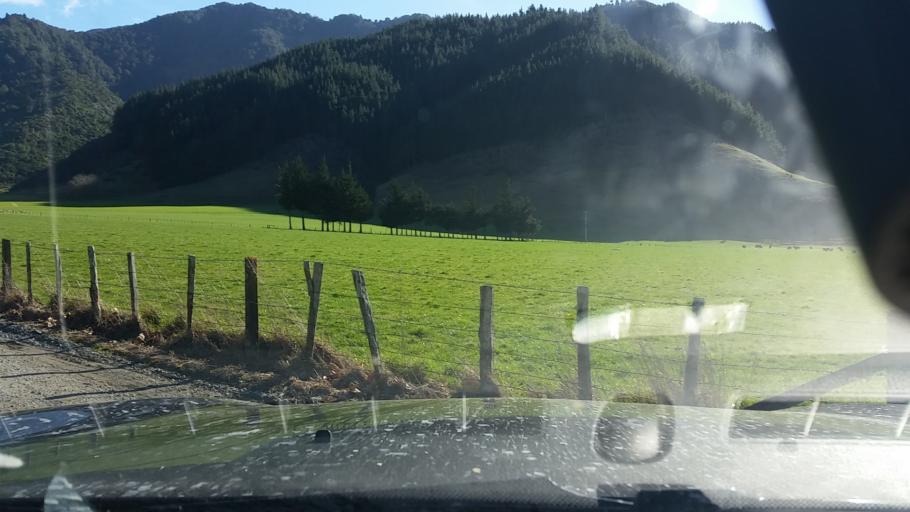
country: NZ
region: Marlborough
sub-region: Marlborough District
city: Picton
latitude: -41.3186
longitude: 173.7649
